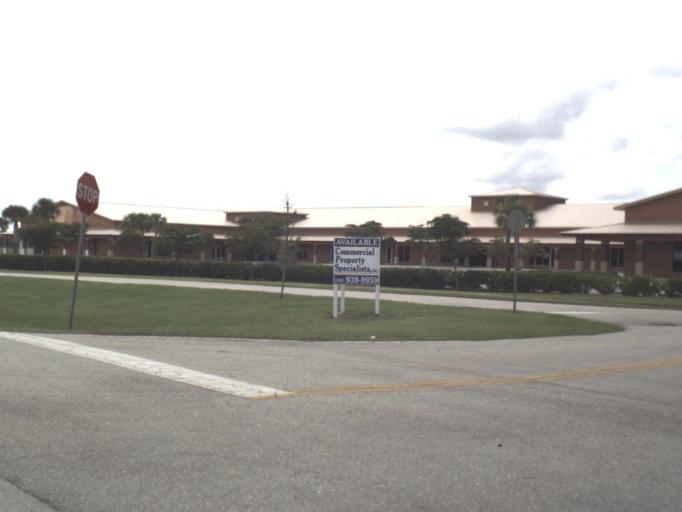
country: US
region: Florida
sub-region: Lee County
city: Pine Manor
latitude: 26.5890
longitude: -81.8533
